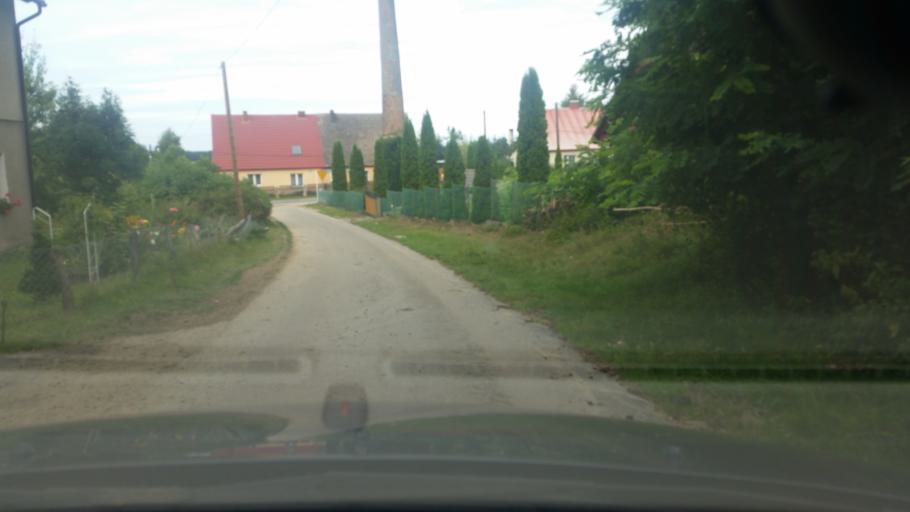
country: PL
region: Pomeranian Voivodeship
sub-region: Powiat leborski
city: Leba
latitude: 54.7263
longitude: 17.6195
